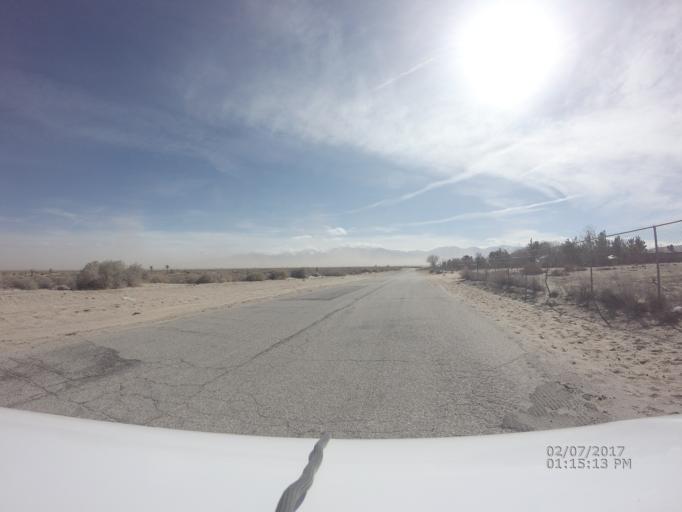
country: US
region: California
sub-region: Los Angeles County
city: Lake Los Angeles
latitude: 34.5908
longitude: -117.8357
